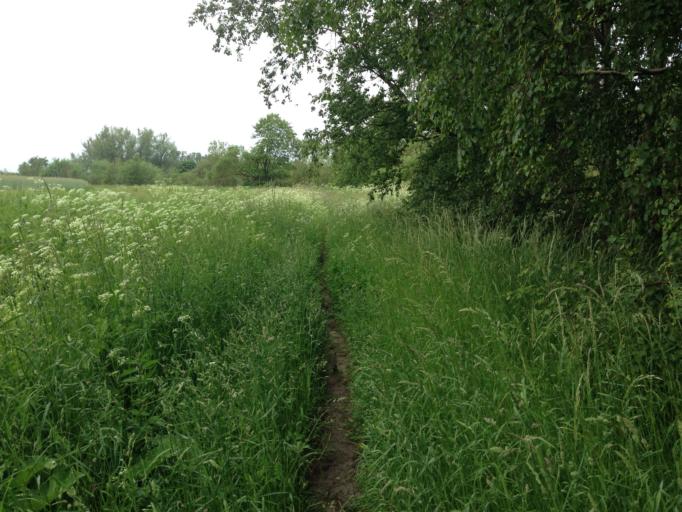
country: SE
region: Skane
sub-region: Lomma Kommun
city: Lomma
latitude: 55.6896
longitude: 13.0784
